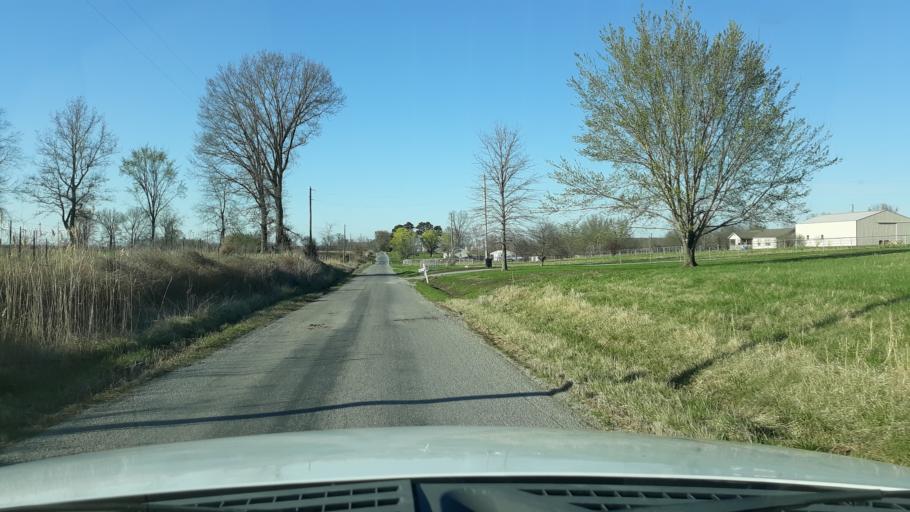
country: US
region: Illinois
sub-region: Saline County
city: Harrisburg
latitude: 37.7786
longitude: -88.6013
